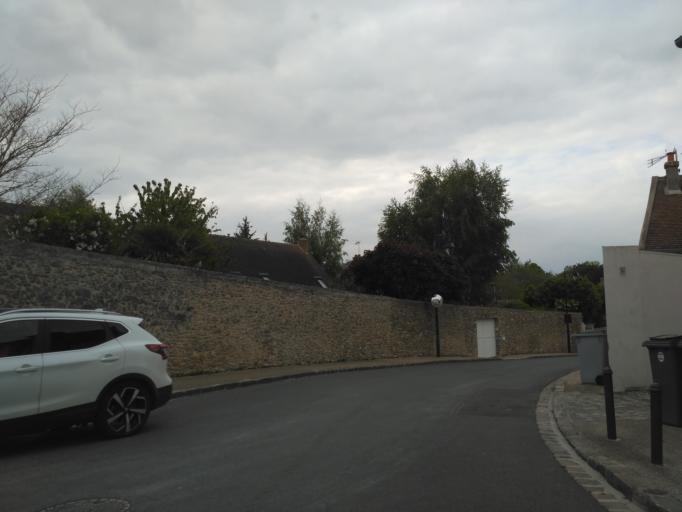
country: FR
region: Ile-de-France
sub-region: Departement de Seine-et-Marne
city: Moisenay
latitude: 48.5681
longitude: 2.7815
